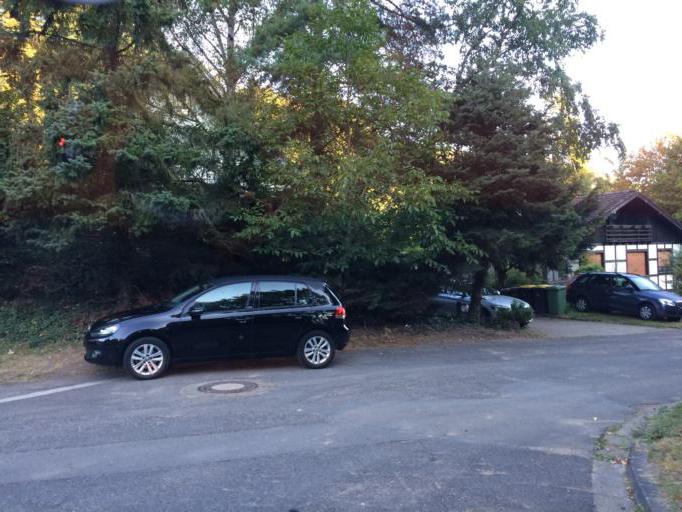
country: DE
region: North Rhine-Westphalia
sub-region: Regierungsbezirk Koln
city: Konigswinter
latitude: 50.6369
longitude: 7.1709
